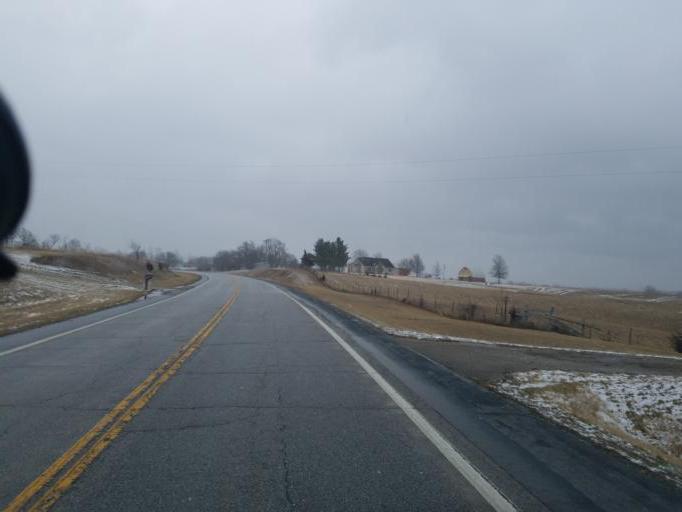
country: US
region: Missouri
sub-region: Putnam County
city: Unionville
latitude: 40.4665
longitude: -92.9251
